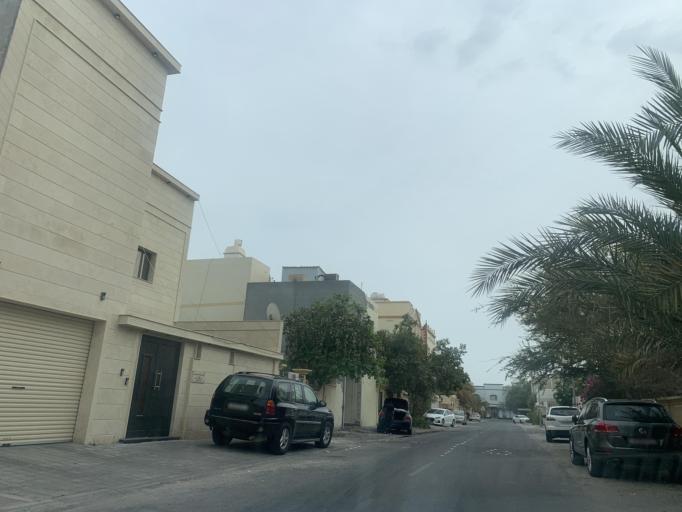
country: BH
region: Muharraq
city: Al Muharraq
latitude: 26.2793
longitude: 50.6399
